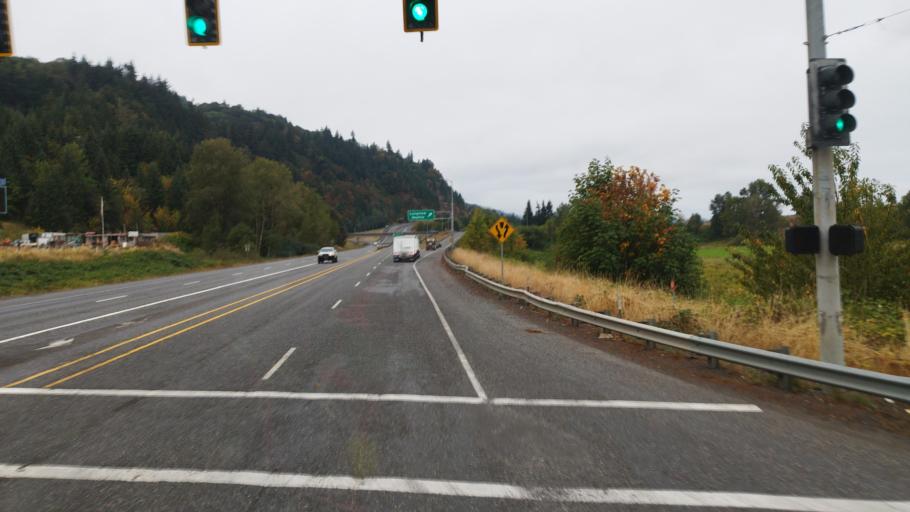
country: US
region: Oregon
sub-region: Columbia County
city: Rainier
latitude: 46.0950
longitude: -122.9635
